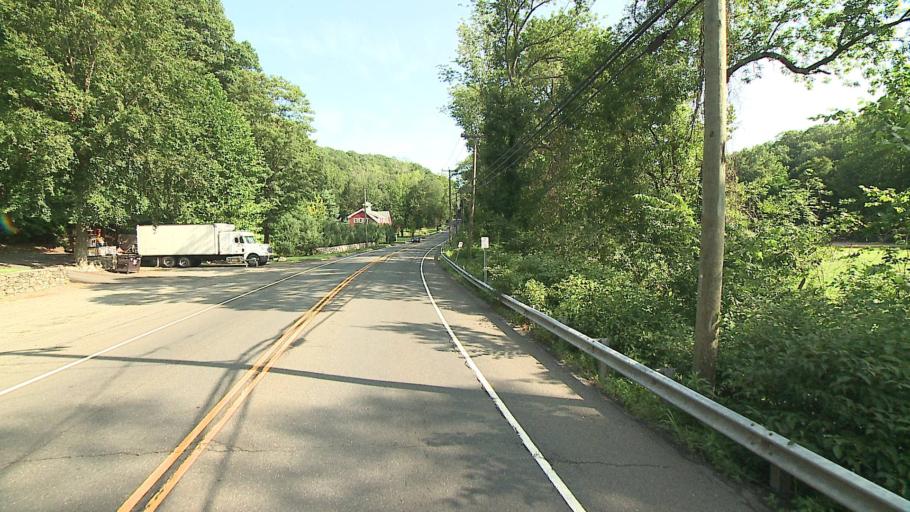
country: US
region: Connecticut
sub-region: Fairfield County
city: Georgetown
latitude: 41.2445
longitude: -73.4343
